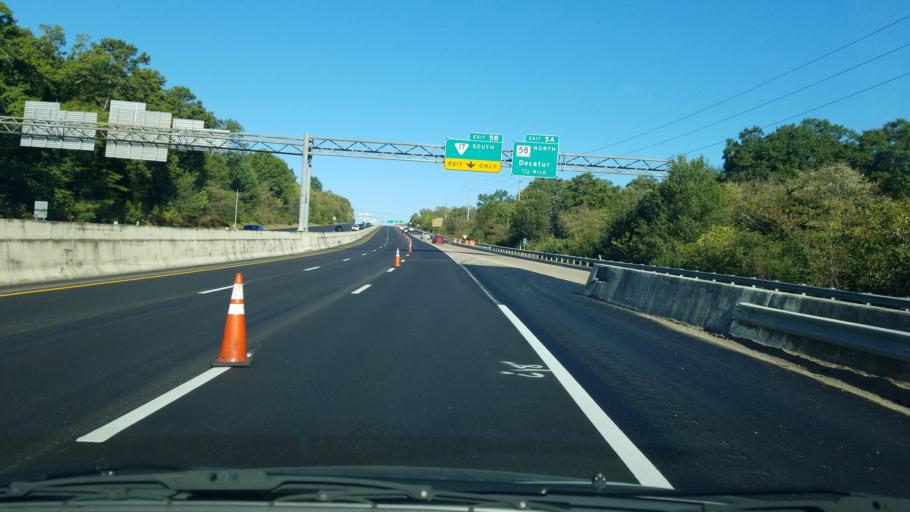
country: US
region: Tennessee
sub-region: Hamilton County
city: East Chattanooga
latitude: 35.0766
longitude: -85.2001
